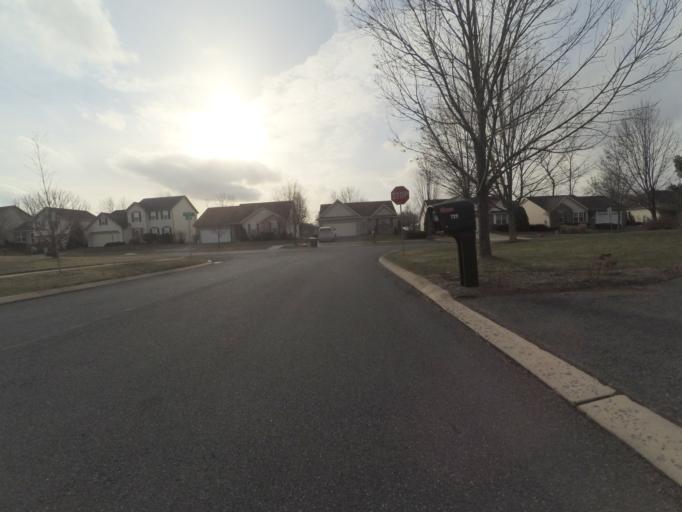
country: US
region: Pennsylvania
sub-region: Centre County
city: Park Forest Village
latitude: 40.7861
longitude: -77.8991
